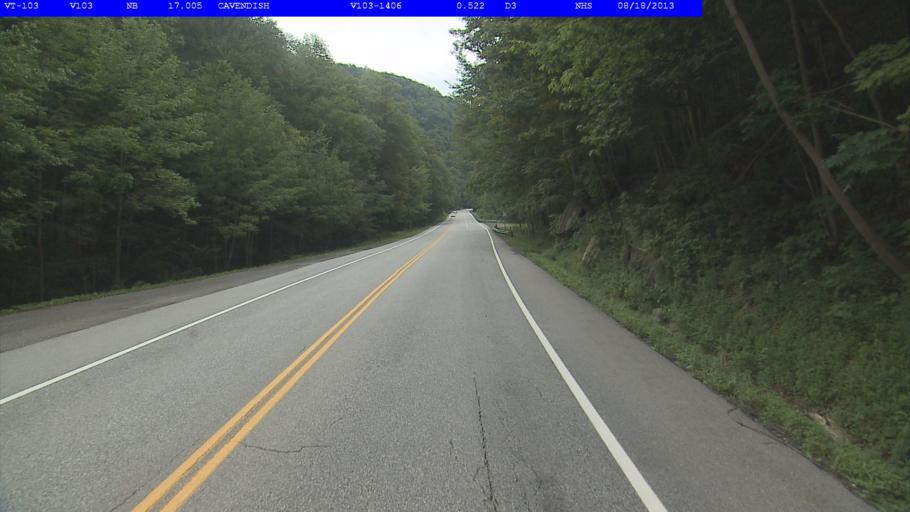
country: US
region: Vermont
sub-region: Windsor County
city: Chester
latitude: 43.3550
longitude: -72.6321
